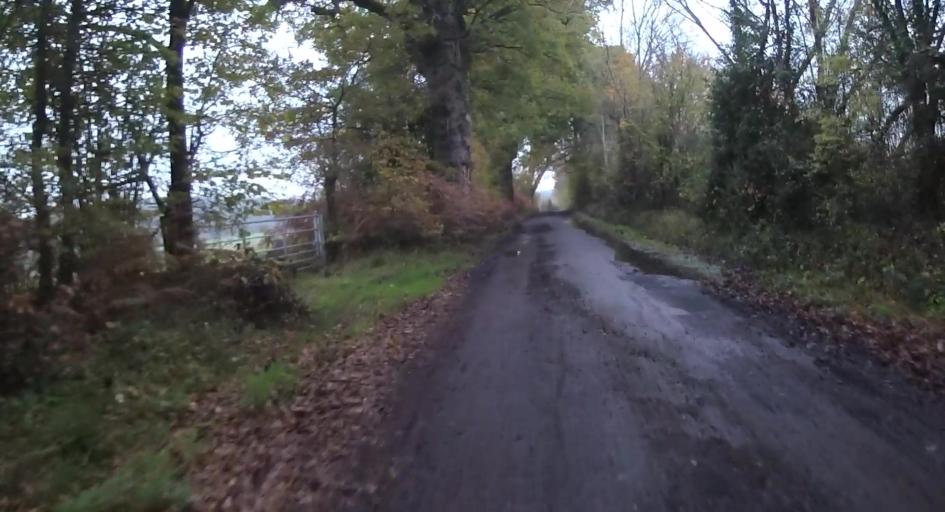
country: GB
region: England
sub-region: Surrey
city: Farnham
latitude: 51.1690
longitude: -0.8205
